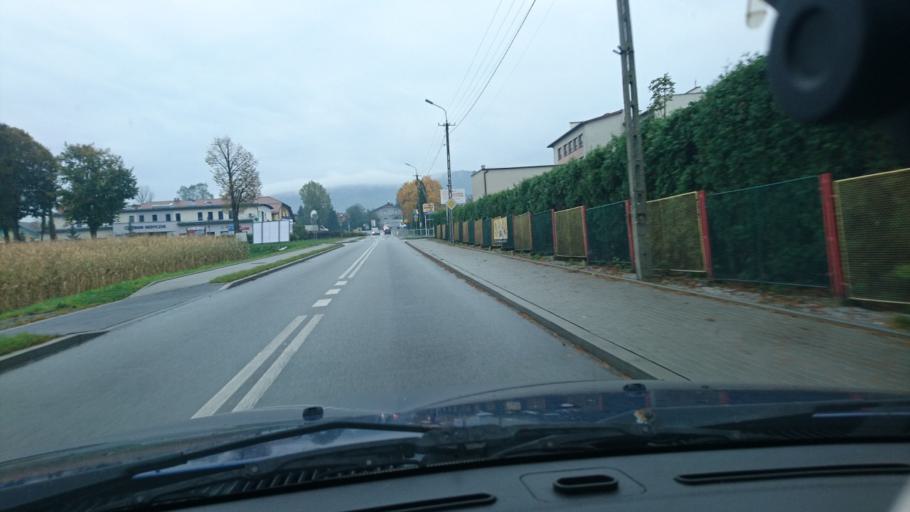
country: PL
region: Silesian Voivodeship
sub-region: Powiat bielski
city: Kozy
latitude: 49.8484
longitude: 19.1461
